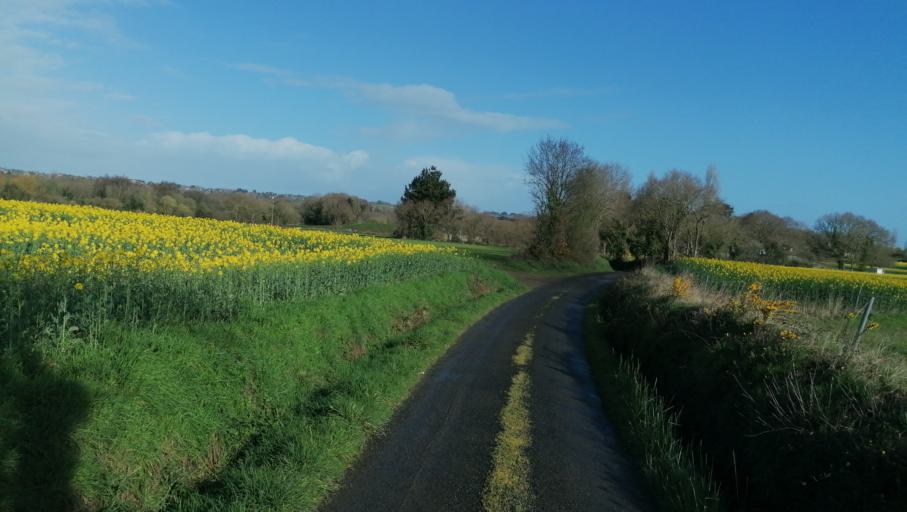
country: FR
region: Brittany
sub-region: Departement des Cotes-d'Armor
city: Plouha
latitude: 48.6527
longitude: -2.9052
